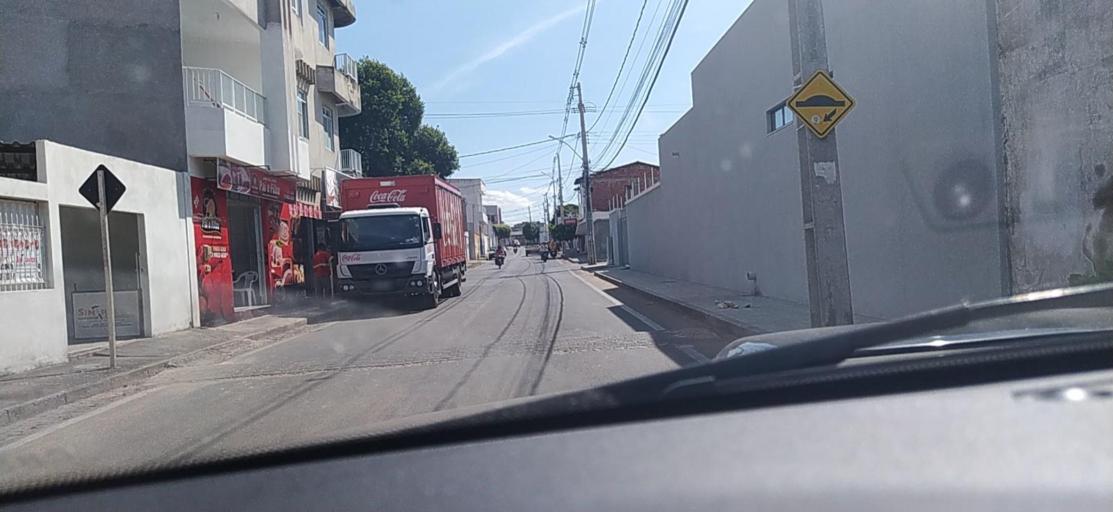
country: BR
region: Bahia
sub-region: Guanambi
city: Guanambi
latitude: -14.2157
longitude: -42.7688
